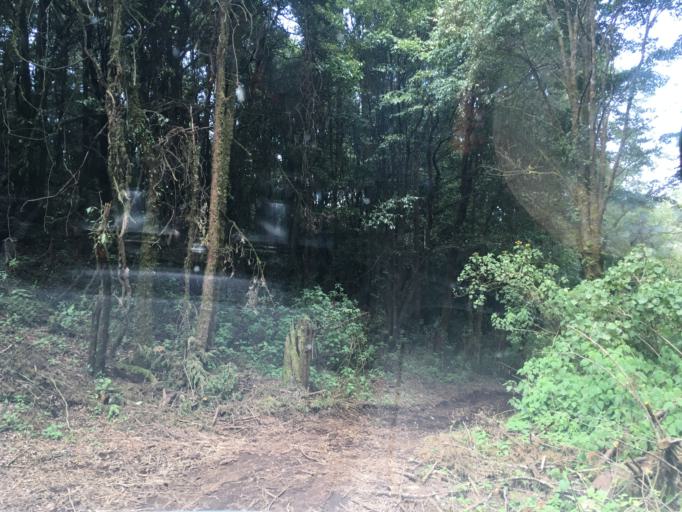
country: MX
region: Michoacan
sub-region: Zitacuaro
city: Francisco Serrato (San Bartolo)
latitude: 19.5087
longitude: -100.3046
